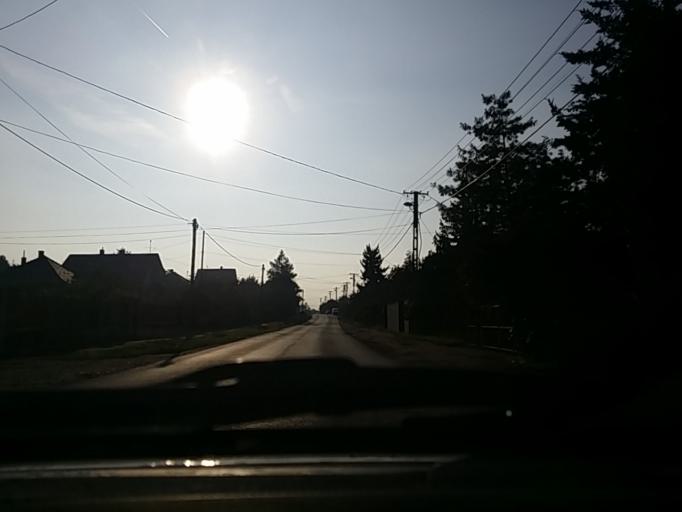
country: HU
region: Pest
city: Szentendre
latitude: 47.6759
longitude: 19.0626
